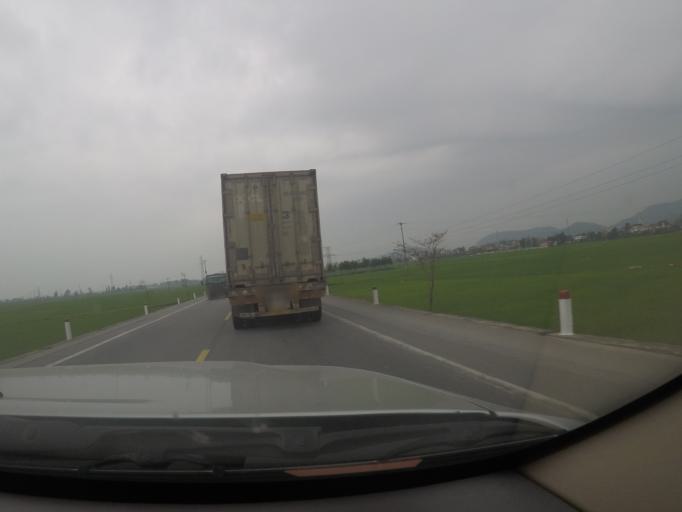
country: VN
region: Nghe An
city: Quan Hanh
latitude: 18.7330
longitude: 105.6320
